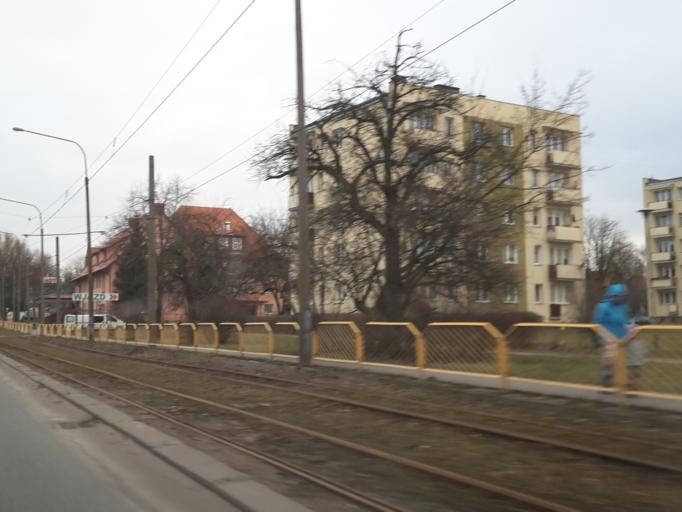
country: PL
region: Warmian-Masurian Voivodeship
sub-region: Powiat elblaski
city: Elblag
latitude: 54.1706
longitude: 19.4116
